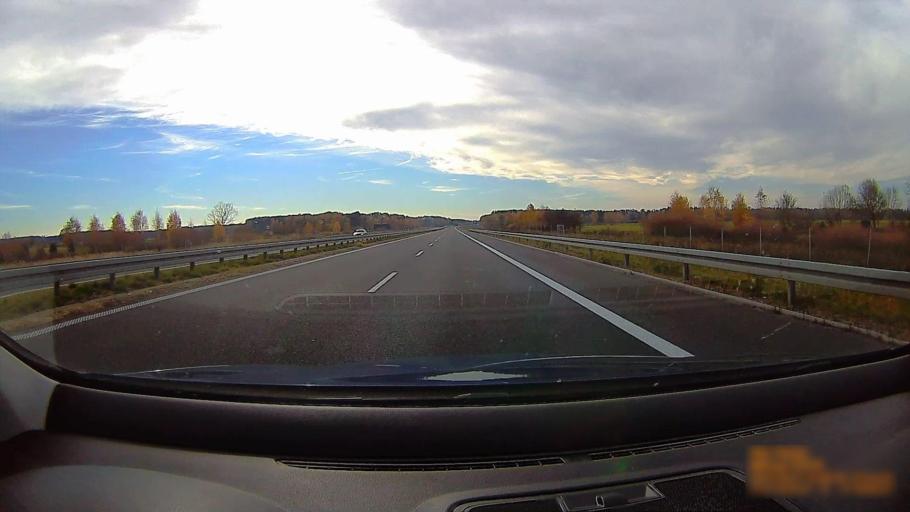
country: PL
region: Greater Poland Voivodeship
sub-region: Powiat ostrowski
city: Przygodzice
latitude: 51.5784
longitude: 17.8491
